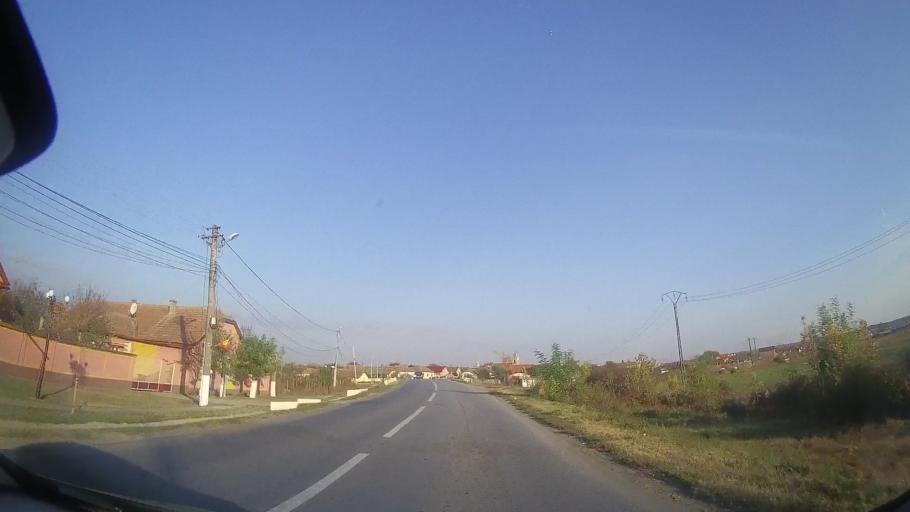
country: RO
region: Timis
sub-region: Comuna Pischia
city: Pischia
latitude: 45.8985
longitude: 21.3422
